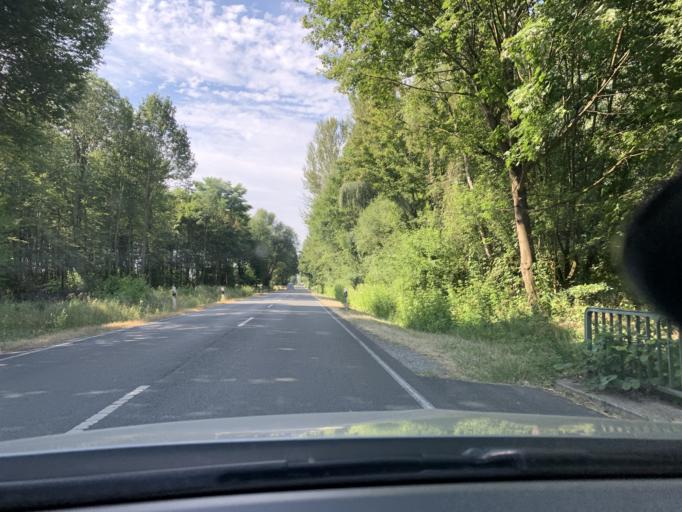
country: DE
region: North Rhine-Westphalia
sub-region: Regierungsbezirk Arnsberg
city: Lippstadt
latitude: 51.7083
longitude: 8.3759
